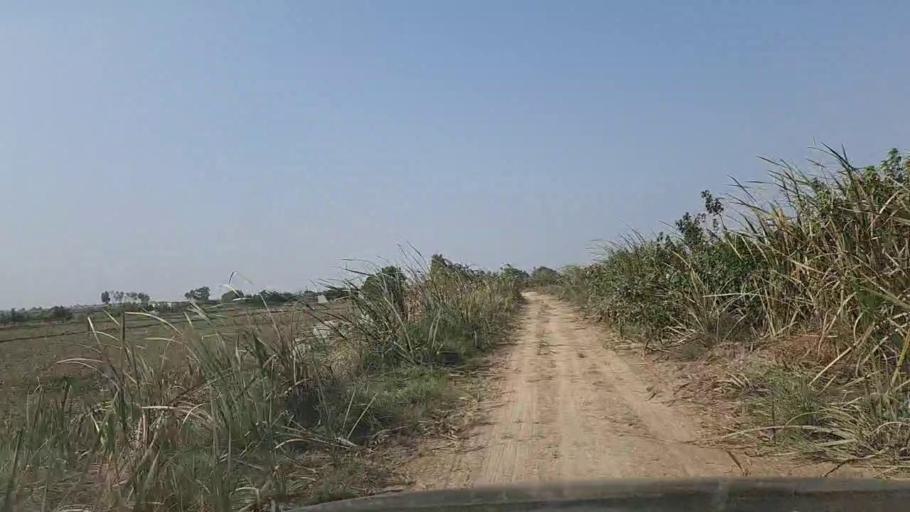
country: PK
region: Sindh
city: Gharo
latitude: 24.7221
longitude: 67.6701
